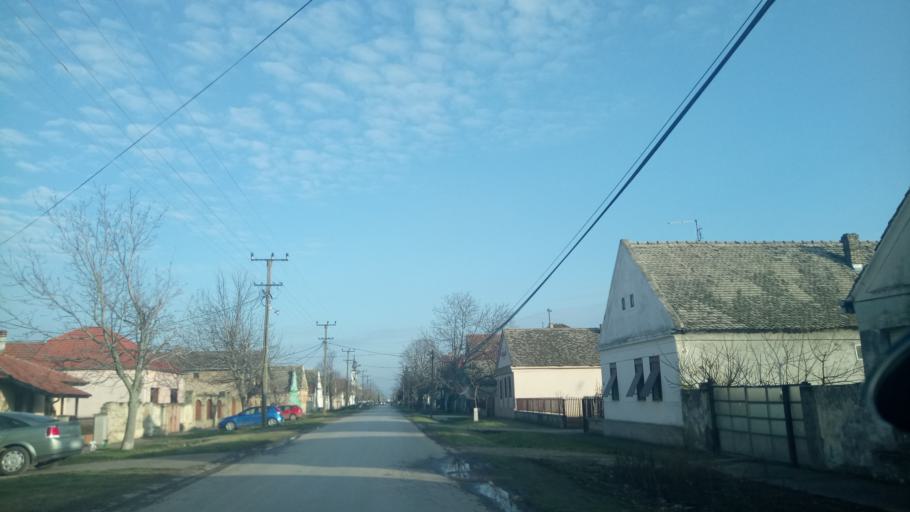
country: RS
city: Vojka
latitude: 44.9361
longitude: 20.1434
